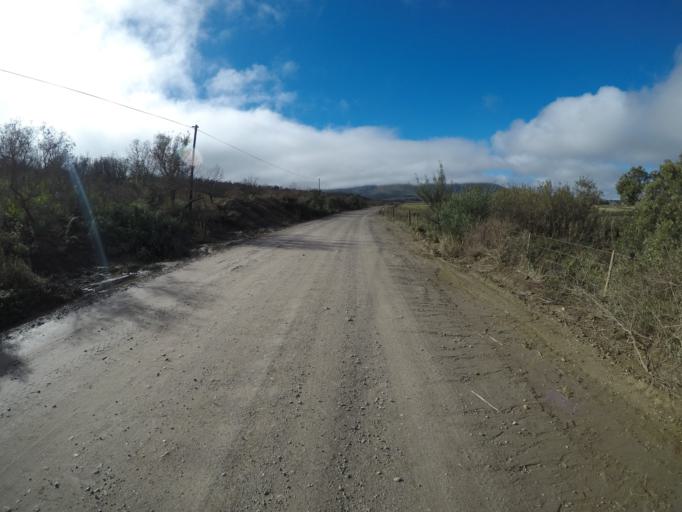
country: ZA
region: Western Cape
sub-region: Cape Winelands District Municipality
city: Ashton
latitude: -34.1225
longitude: 19.8337
